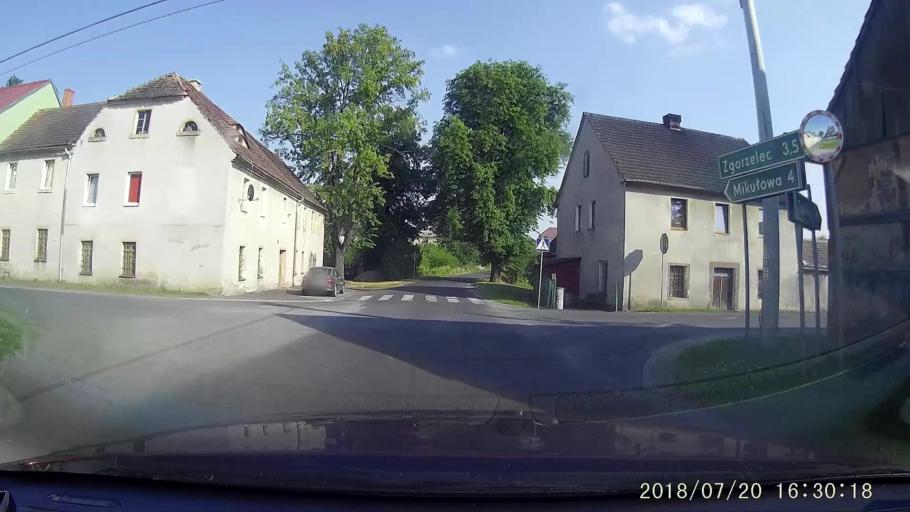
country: PL
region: Lower Silesian Voivodeship
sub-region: Powiat zgorzelecki
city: Sulikow
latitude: 51.1053
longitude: 15.0674
